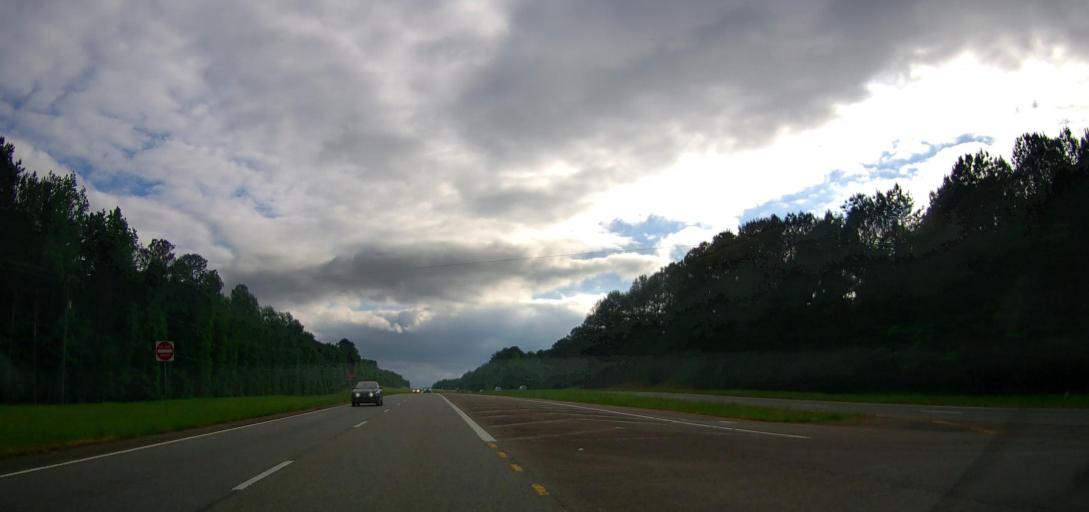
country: US
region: Georgia
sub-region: Oconee County
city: Bogart
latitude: 33.9069
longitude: -83.5647
